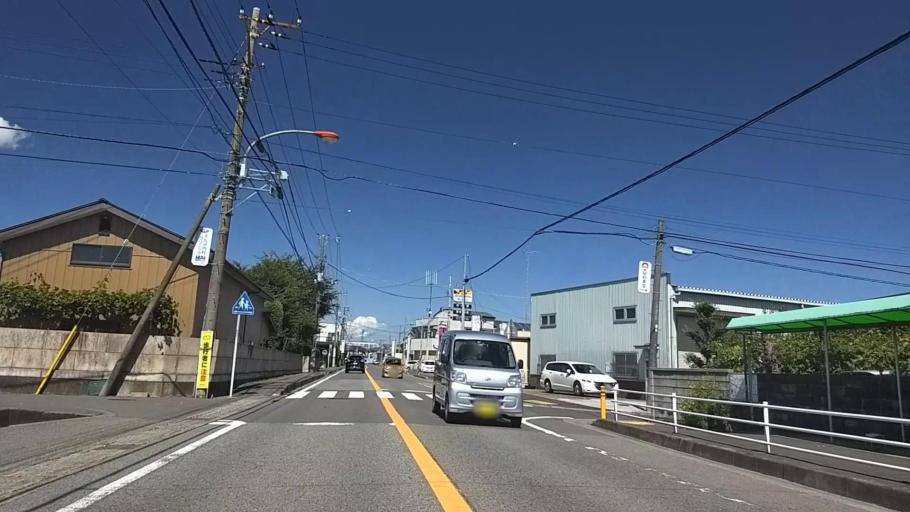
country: JP
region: Kanagawa
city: Zama
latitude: 35.5600
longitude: 139.3271
